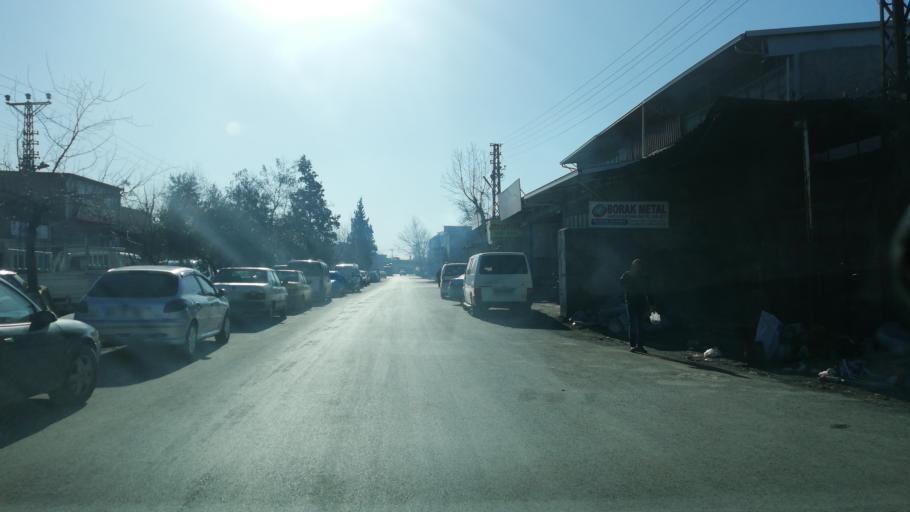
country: TR
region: Kahramanmaras
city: Kahramanmaras
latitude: 37.5601
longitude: 36.9586
